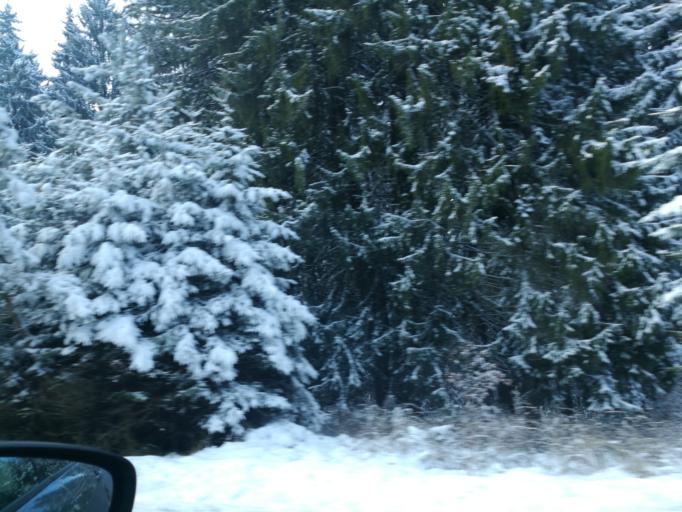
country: RO
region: Brasov
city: Brasov
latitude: 45.6130
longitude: 25.5465
